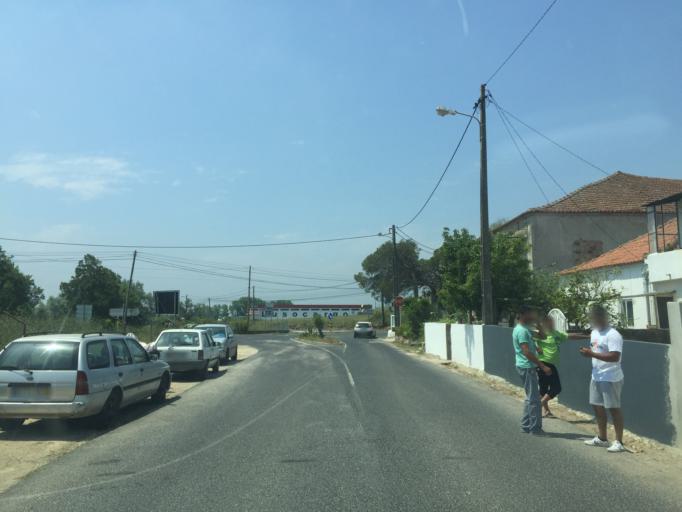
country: PT
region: Lisbon
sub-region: Mafra
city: Milharado
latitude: 38.8974
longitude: -9.1859
